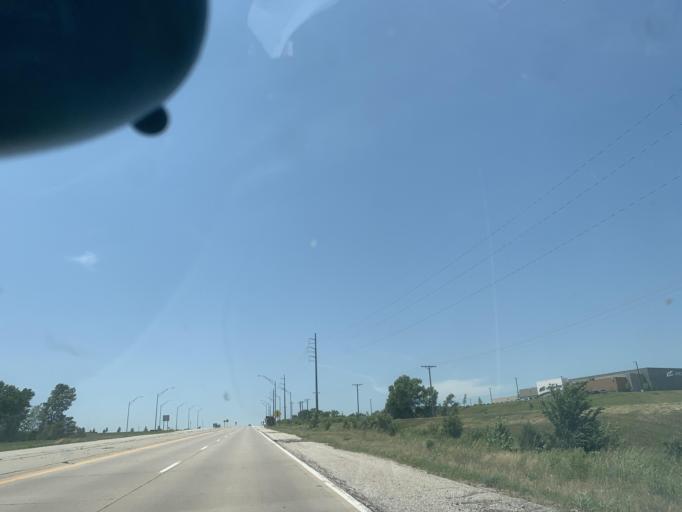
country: US
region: Nebraska
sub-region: Douglas County
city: Elkhorn
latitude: 41.2339
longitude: -96.2367
